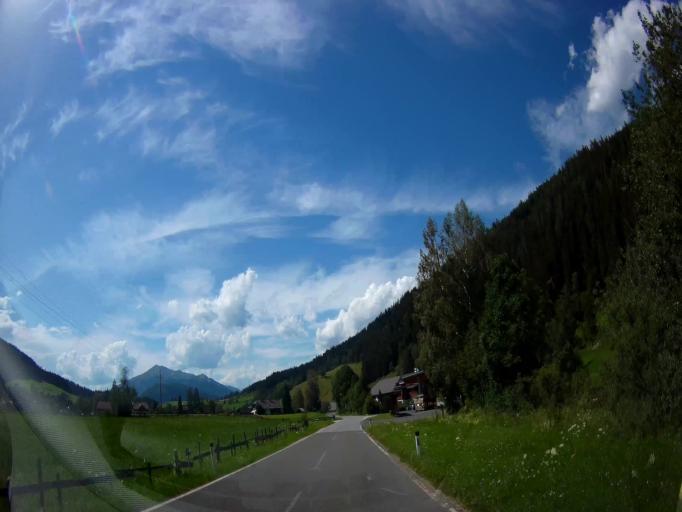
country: AT
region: Salzburg
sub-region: Politischer Bezirk Tamsweg
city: Thomatal
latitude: 47.0745
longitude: 13.7420
